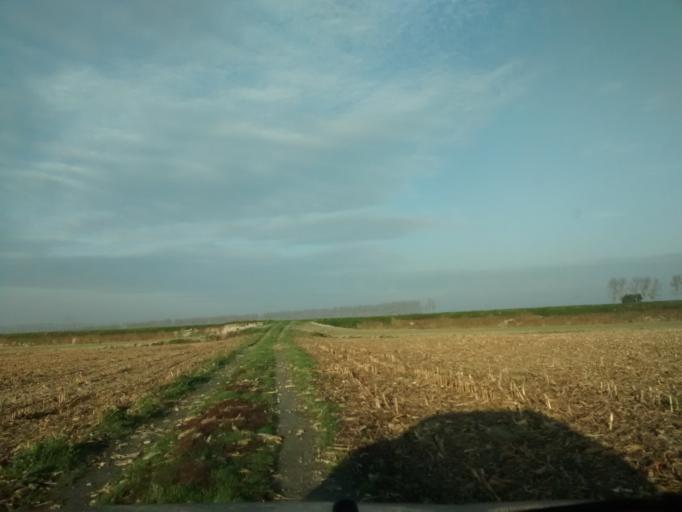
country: FR
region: Brittany
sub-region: Departement d'Ille-et-Vilaine
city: Roz-sur-Couesnon
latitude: 48.6151
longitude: -1.5615
